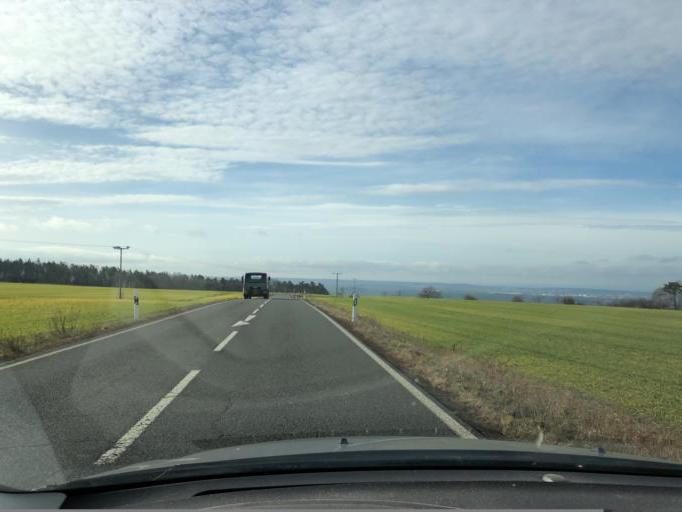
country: DE
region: Thuringia
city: Ballstedt
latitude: 51.0322
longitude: 11.2251
